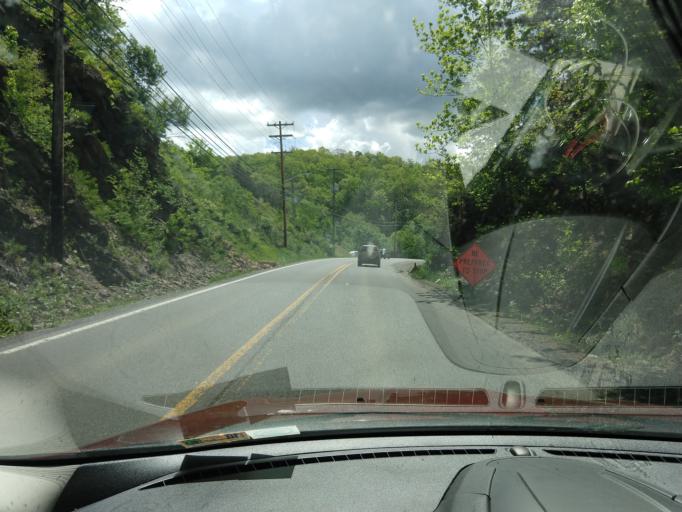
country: US
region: West Virginia
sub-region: Mercer County
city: Bluefield
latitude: 37.2607
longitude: -81.2355
